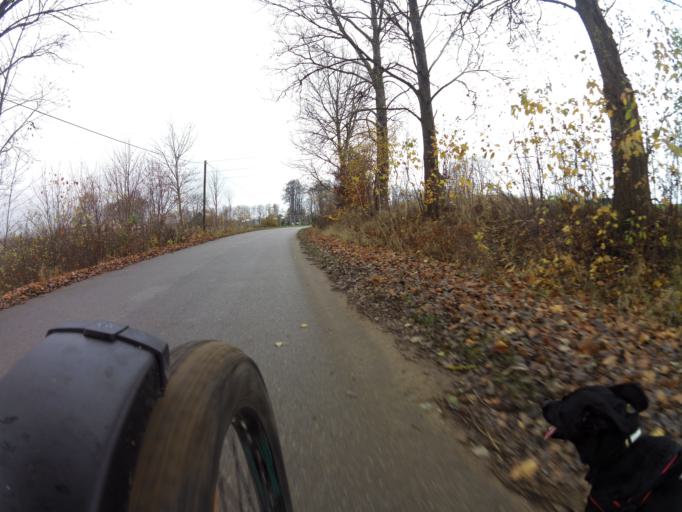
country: PL
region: Pomeranian Voivodeship
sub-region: Powiat pucki
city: Krokowa
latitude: 54.7219
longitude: 18.1379
